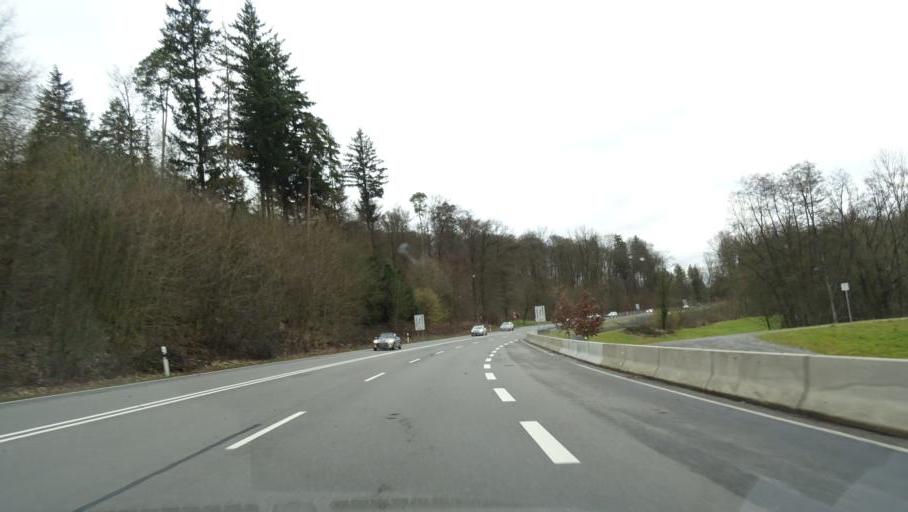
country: DE
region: Baden-Wuerttemberg
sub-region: Karlsruhe Region
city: Aglasterhausen
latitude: 49.3327
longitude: 8.9741
